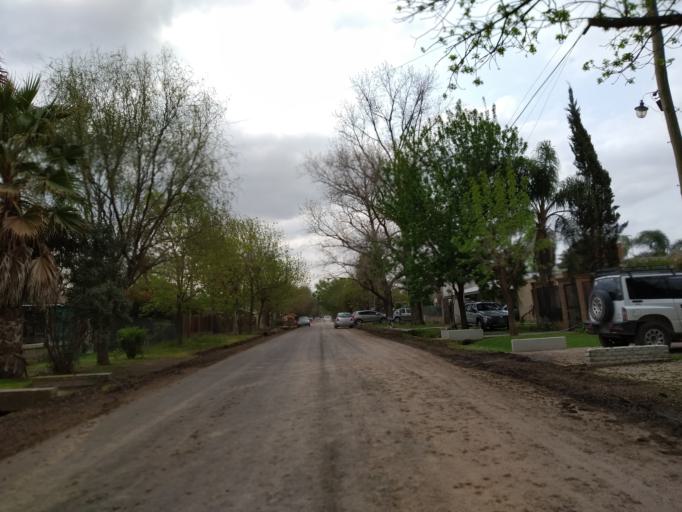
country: AR
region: Santa Fe
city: Funes
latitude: -32.9235
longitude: -60.8511
